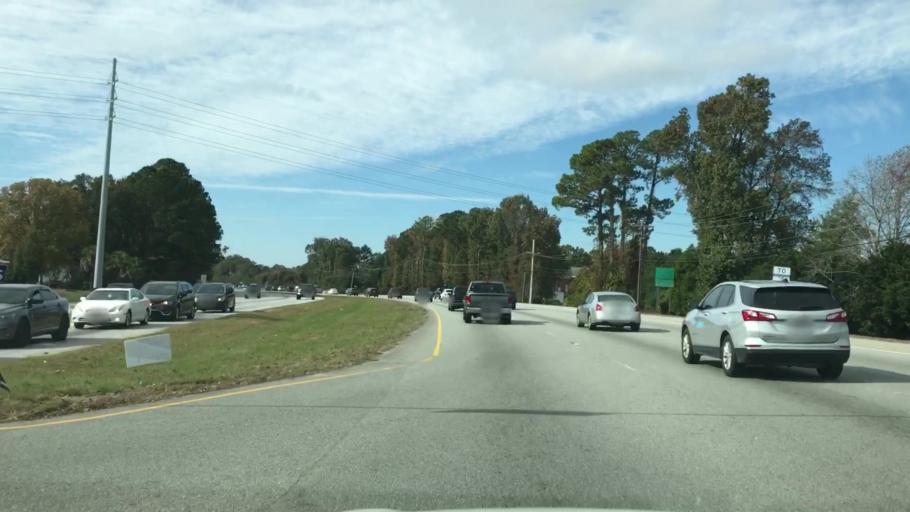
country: US
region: South Carolina
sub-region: Charleston County
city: Shell Point
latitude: 32.8123
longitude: -80.0440
